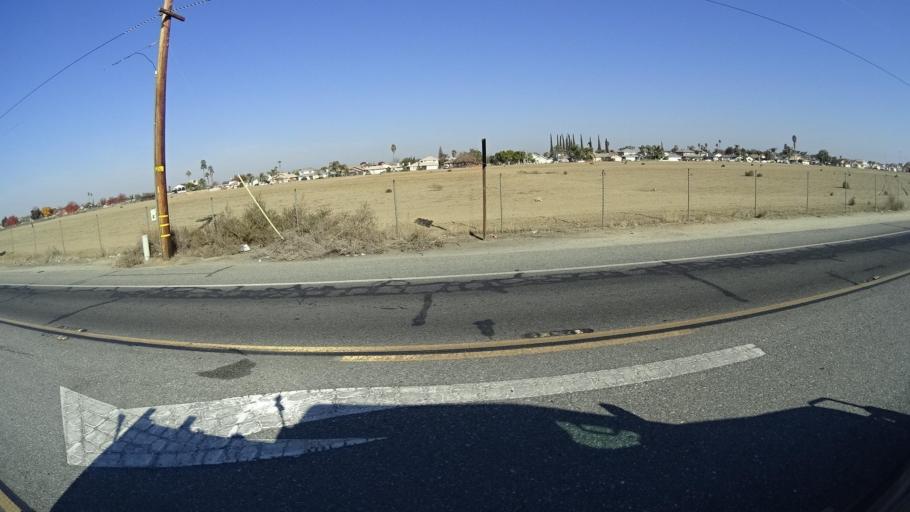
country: US
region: California
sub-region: Kern County
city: Delano
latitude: 35.7617
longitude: -119.2300
